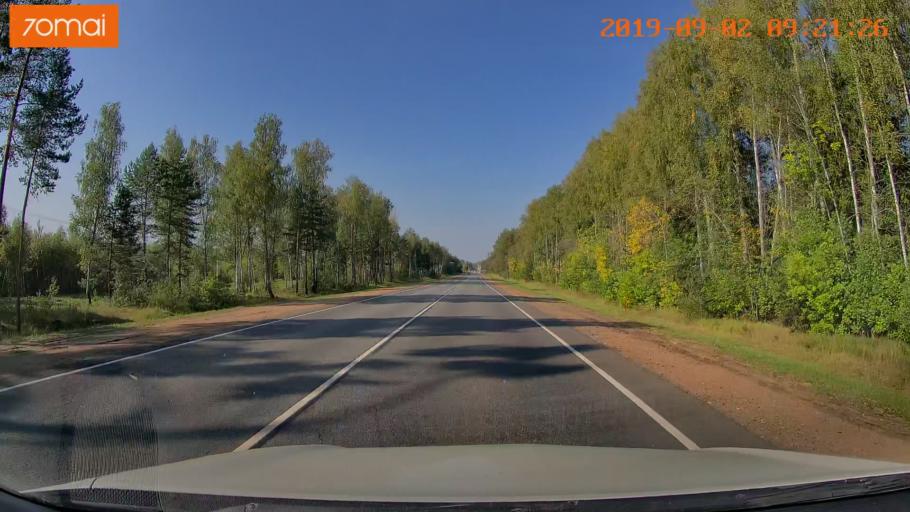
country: RU
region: Kaluga
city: Yukhnov
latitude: 54.7919
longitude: 35.3593
